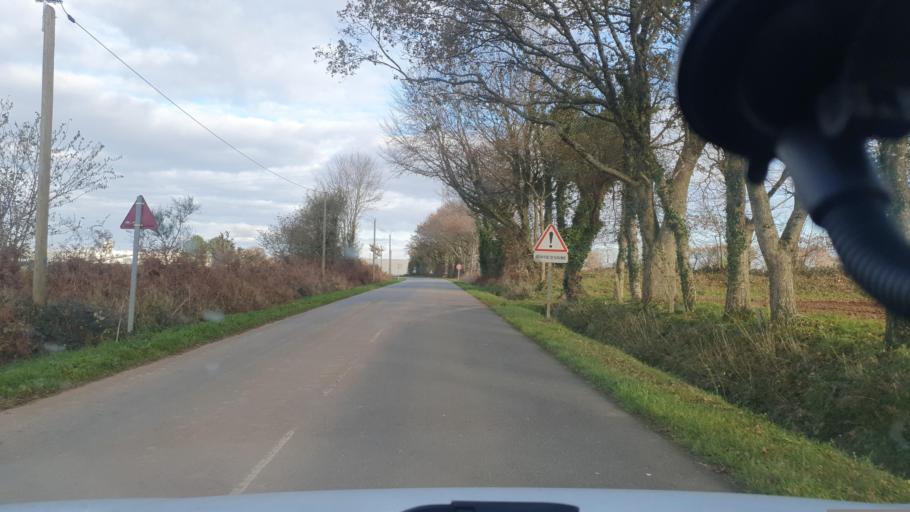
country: FR
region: Brittany
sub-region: Departement du Finistere
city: Briec
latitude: 48.0947
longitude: -4.0248
